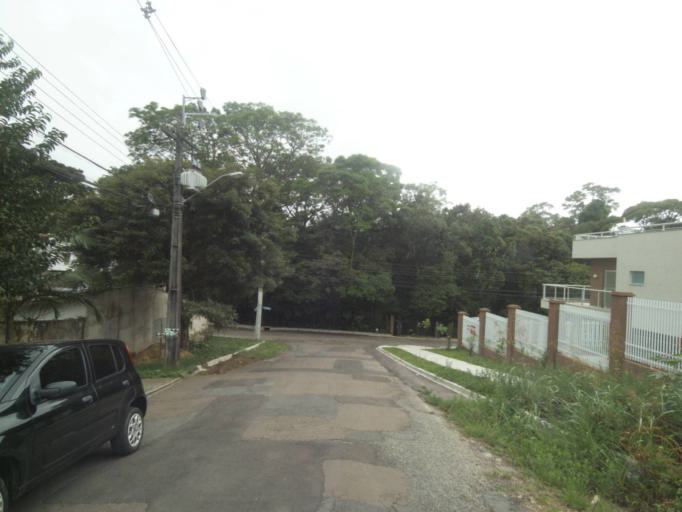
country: BR
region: Parana
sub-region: Curitiba
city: Curitiba
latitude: -25.3960
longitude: -49.2787
